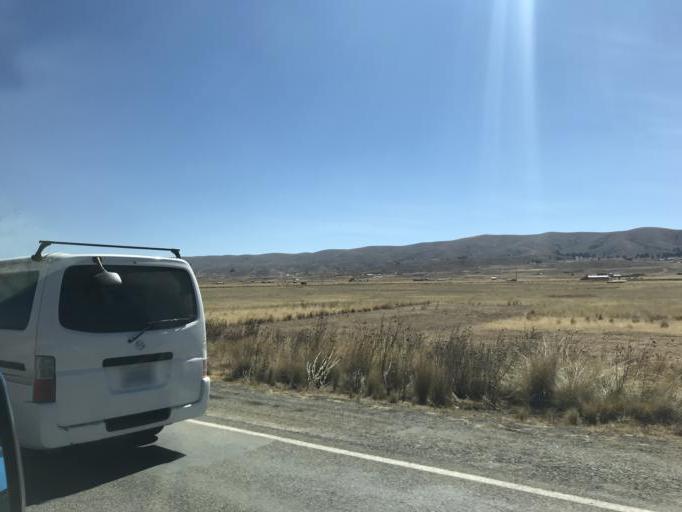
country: BO
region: La Paz
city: Tiahuanaco
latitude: -16.5922
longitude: -68.5813
